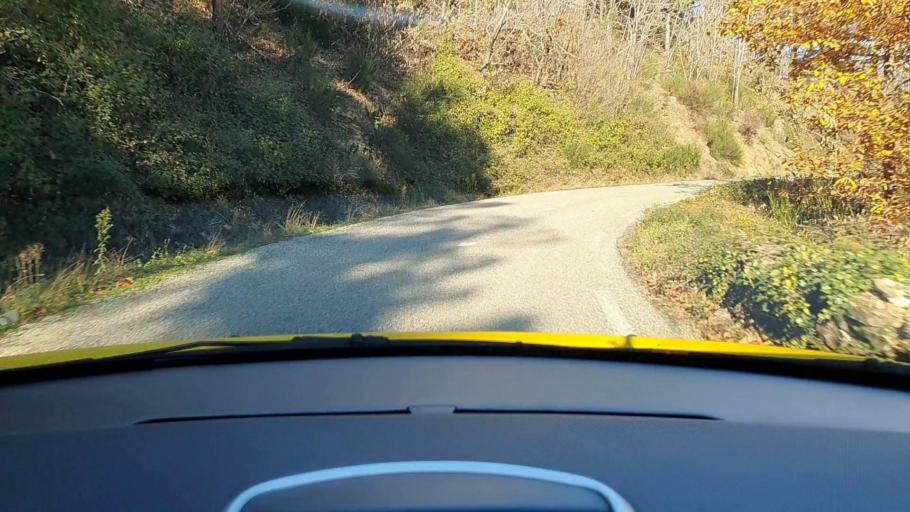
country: FR
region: Languedoc-Roussillon
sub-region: Departement du Gard
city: Branoux-les-Taillades
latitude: 44.2848
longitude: 3.9787
